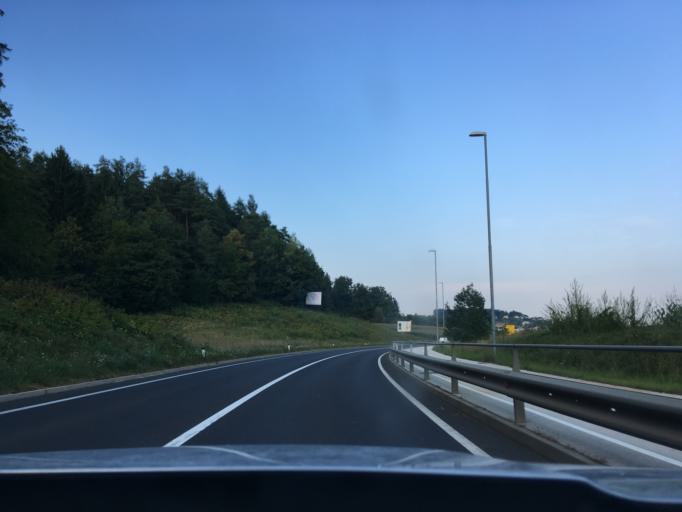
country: SI
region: Novo Mesto
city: Novo Mesto
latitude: 45.8248
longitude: 15.1755
